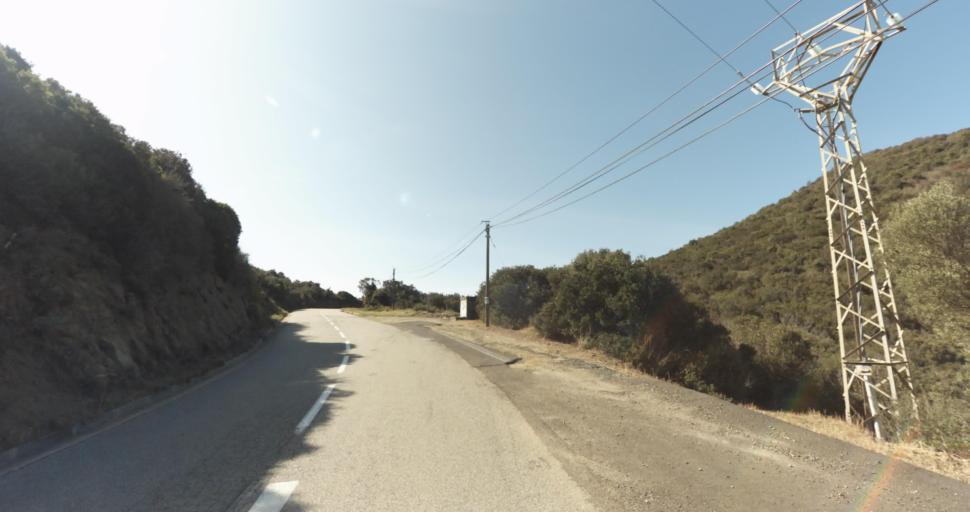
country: FR
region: Corsica
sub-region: Departement de la Corse-du-Sud
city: Ajaccio
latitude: 41.9231
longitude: 8.6425
